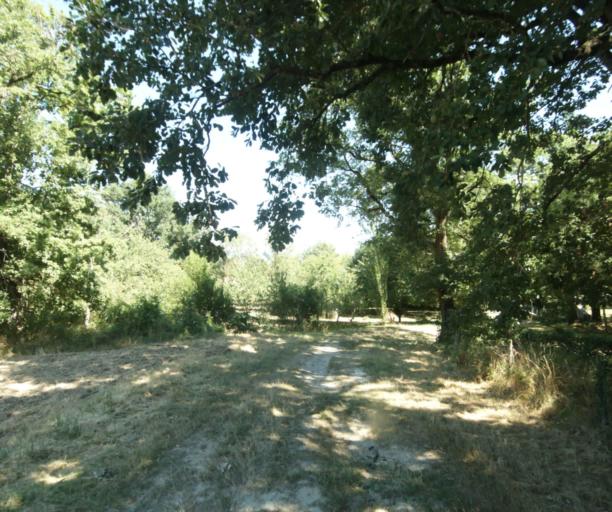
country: FR
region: Midi-Pyrenees
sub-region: Departement de la Haute-Garonne
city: Saint-Felix-Lauragais
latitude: 43.4832
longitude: 1.9232
